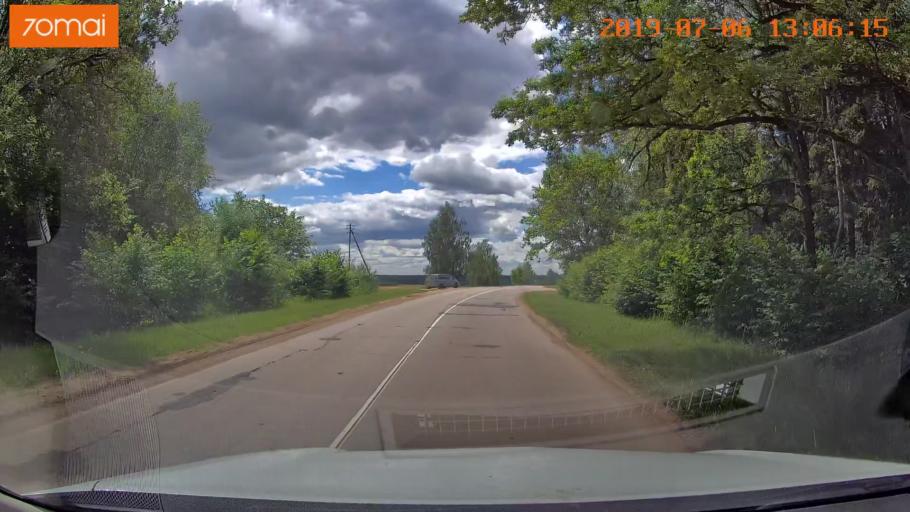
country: BY
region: Minsk
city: Dzyarzhynsk
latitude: 53.6826
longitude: 27.0561
